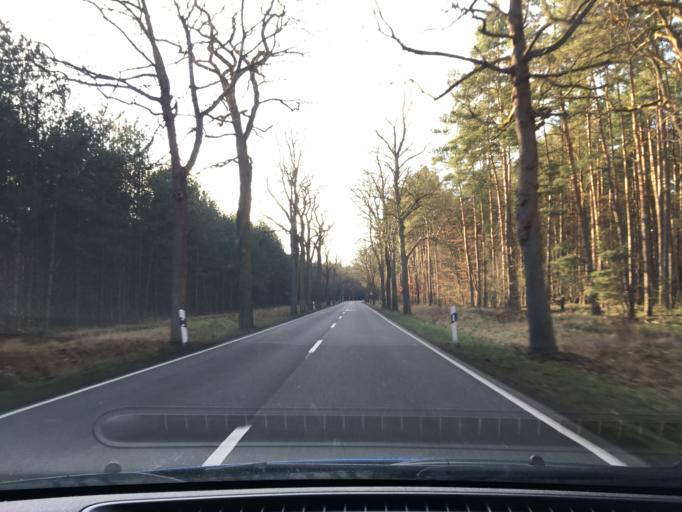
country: DE
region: Saxony-Anhalt
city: Seehausen
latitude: 52.8833
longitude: 11.6271
